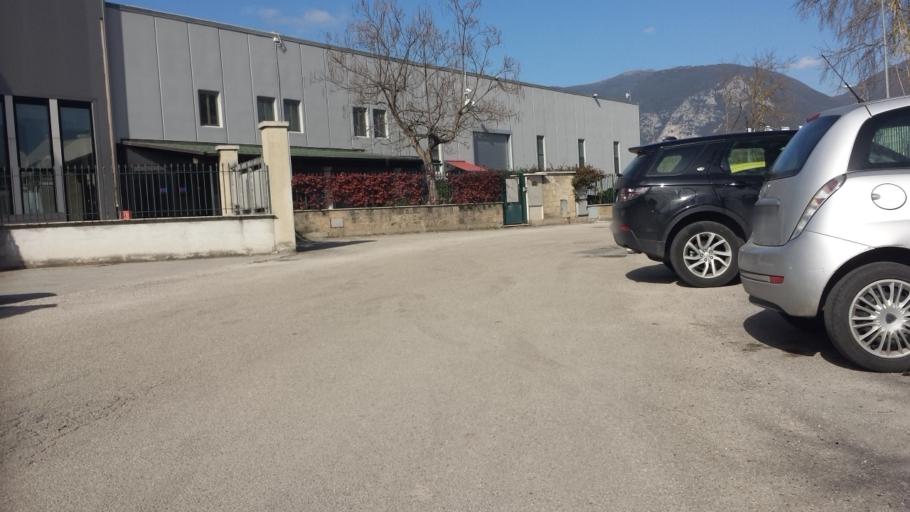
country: IT
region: Umbria
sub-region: Provincia di Terni
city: Terni
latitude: 42.5656
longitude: 12.5994
